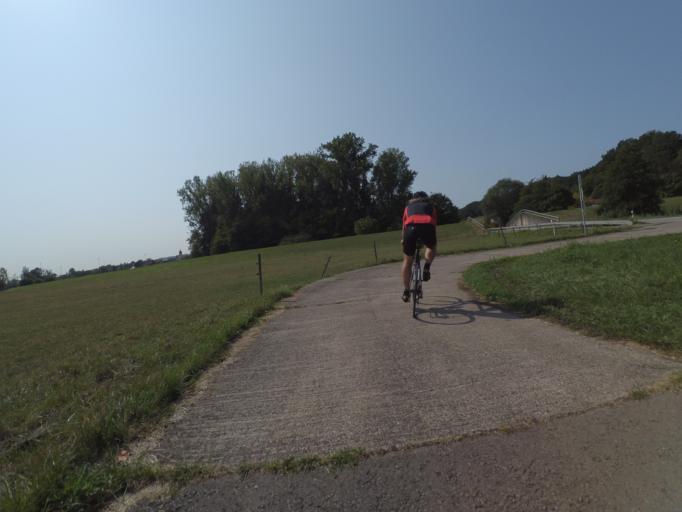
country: DE
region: Saarland
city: Mettlach
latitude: 49.4721
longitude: 6.5905
